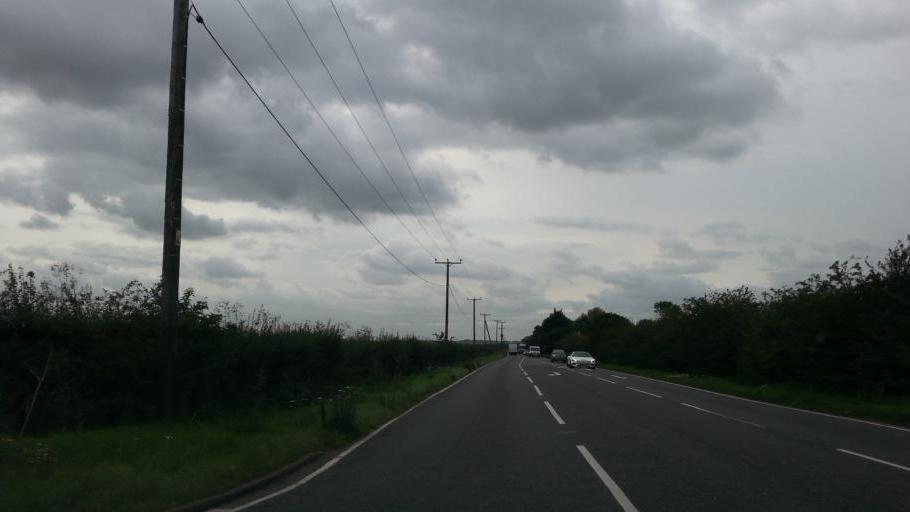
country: GB
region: England
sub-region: Cambridgeshire
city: Melbourn
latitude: 52.0737
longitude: 0.0772
